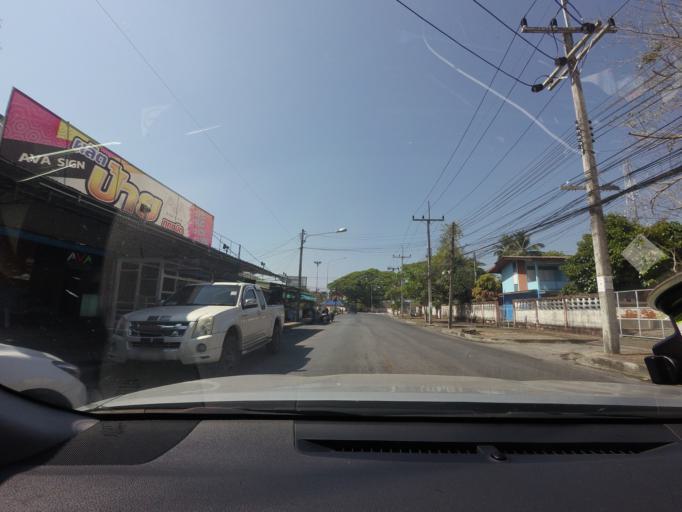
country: TH
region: Yala
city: Yala
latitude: 6.5454
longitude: 101.2856
